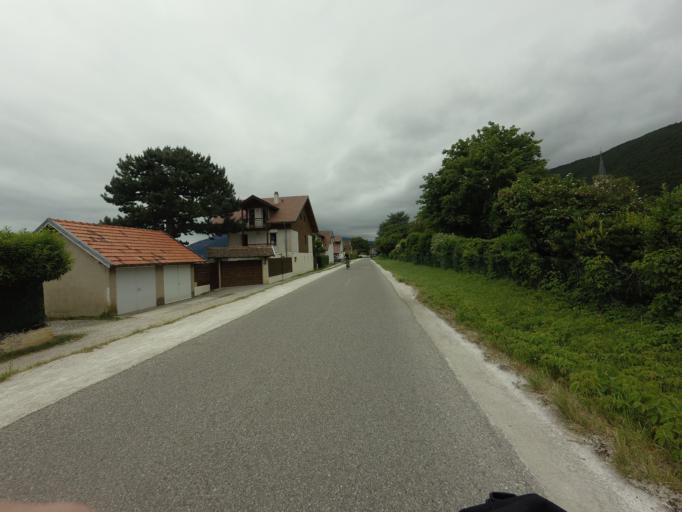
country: FR
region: Rhone-Alpes
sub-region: Departement de la Haute-Savoie
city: Sevrier
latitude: 45.8651
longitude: 6.1438
